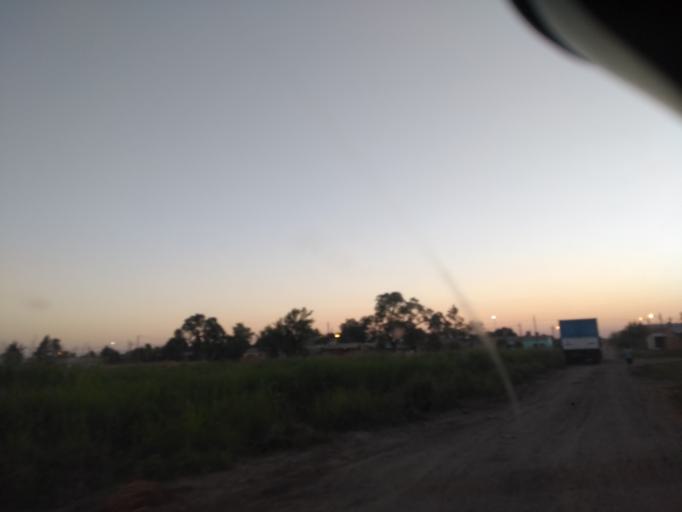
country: AR
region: Chaco
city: Fontana
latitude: -27.4168
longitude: -59.0448
